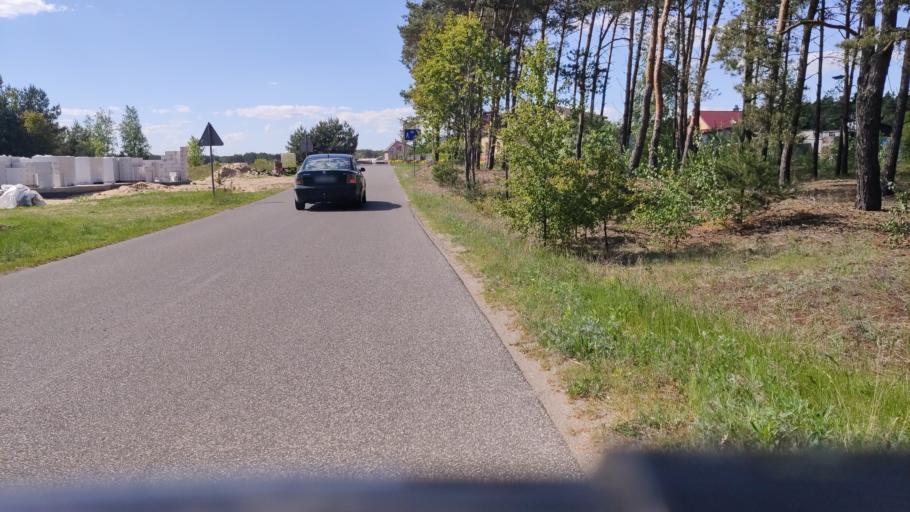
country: PL
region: Kujawsko-Pomorskie
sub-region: Wloclawek
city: Wloclawek
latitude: 52.5901
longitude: 19.0934
